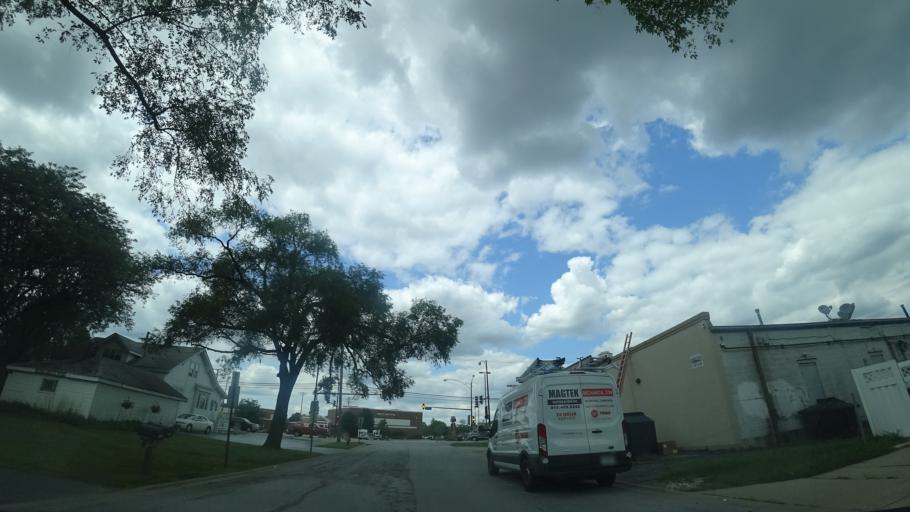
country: US
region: Illinois
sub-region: Cook County
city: Alsip
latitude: 41.6833
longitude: -87.7224
